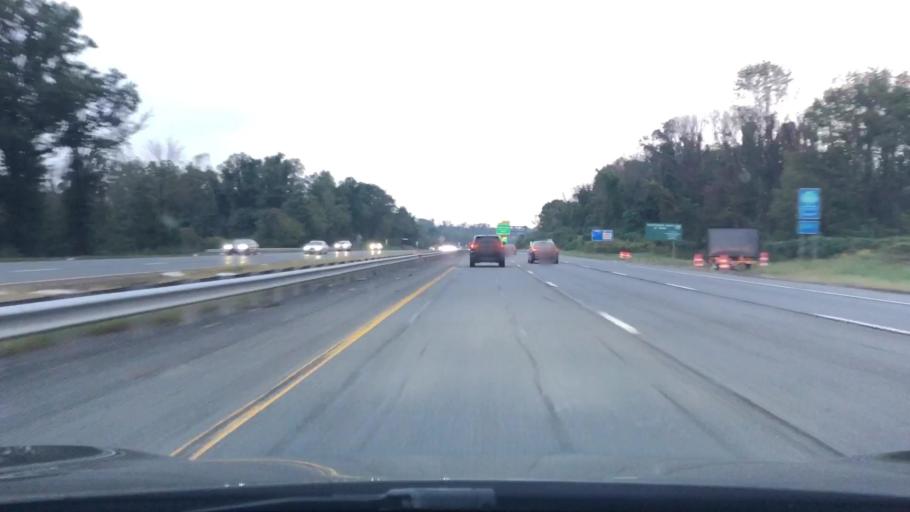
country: US
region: New Jersey
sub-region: Mercer County
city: Ewing
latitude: 40.2813
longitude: -74.8232
